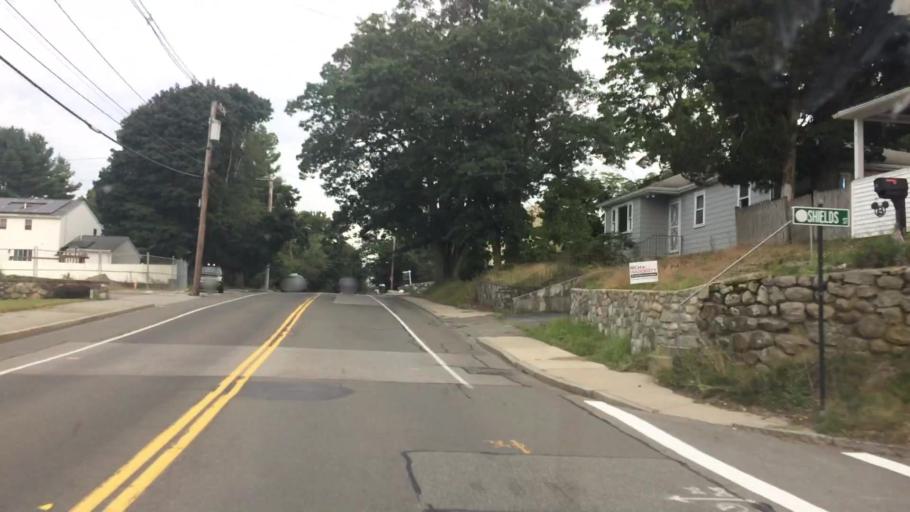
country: US
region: Massachusetts
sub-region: Middlesex County
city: Woburn
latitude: 42.4867
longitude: -71.1641
